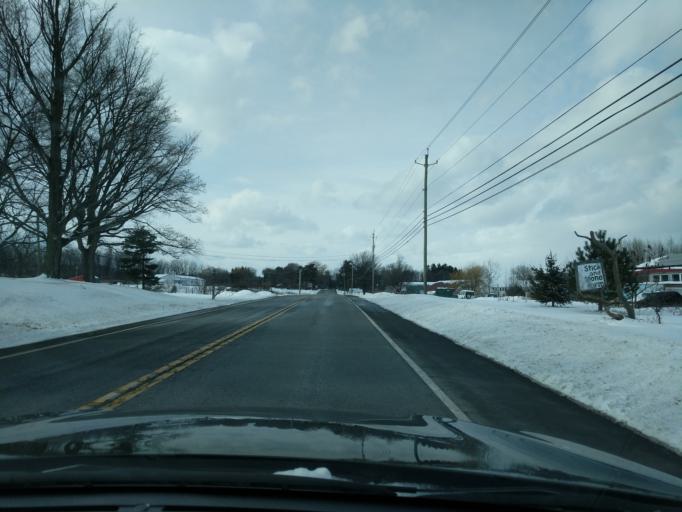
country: US
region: New York
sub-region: Tompkins County
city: Northwest Ithaca
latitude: 42.4868
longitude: -76.5758
